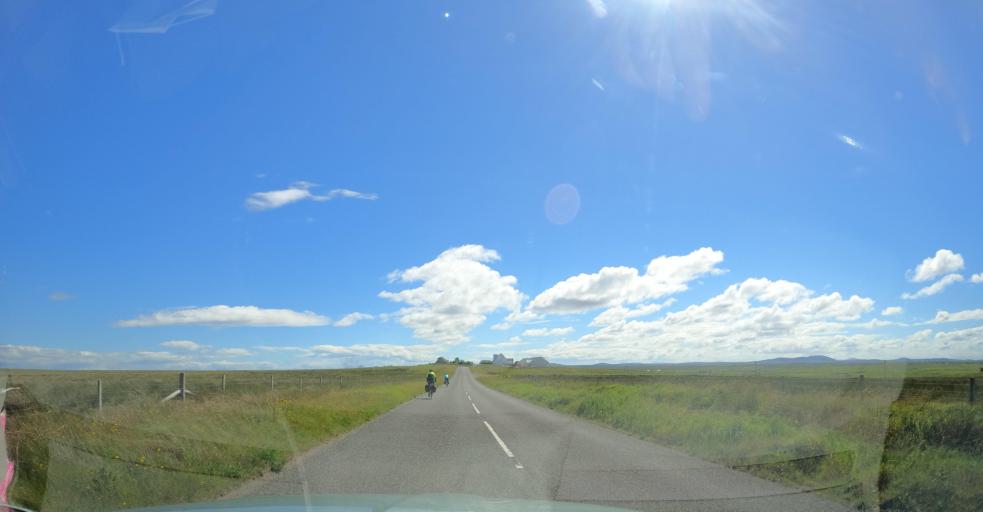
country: GB
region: Scotland
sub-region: Eilean Siar
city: Isle of Lewis
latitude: 58.3725
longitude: -6.5054
